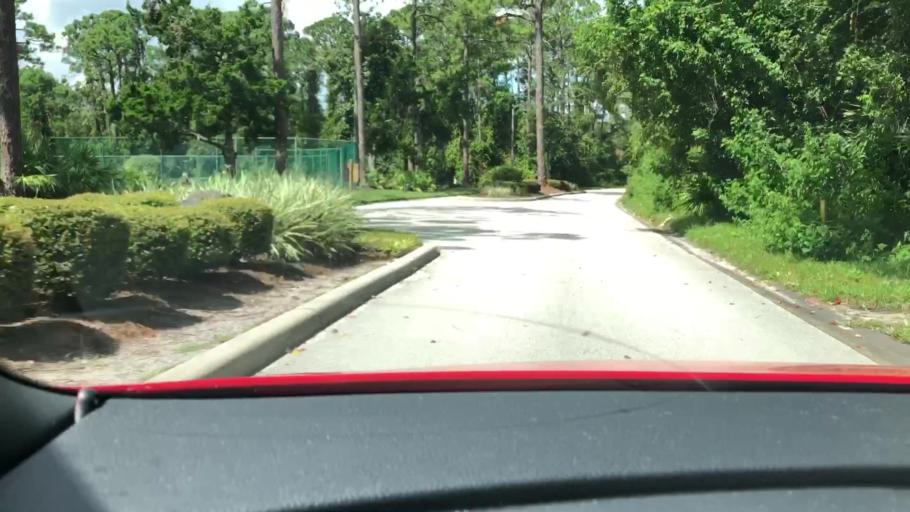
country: US
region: Florida
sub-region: Volusia County
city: Ormond Beach
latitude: 29.2696
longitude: -81.0970
